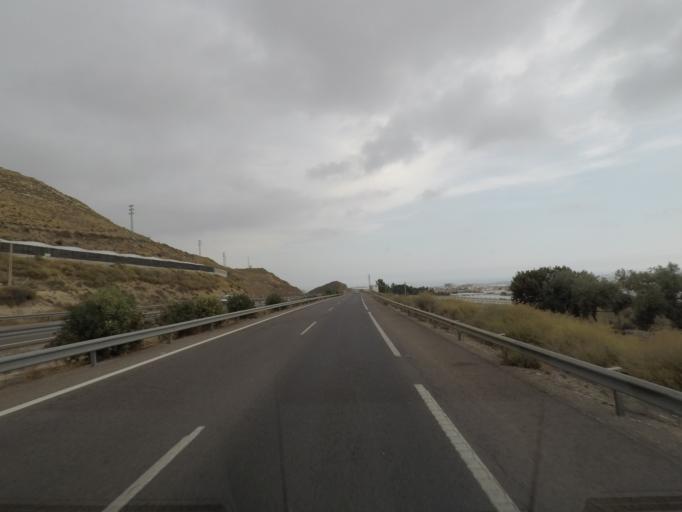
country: ES
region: Andalusia
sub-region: Provincia de Almeria
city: Vicar
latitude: 36.8126
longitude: -2.6408
